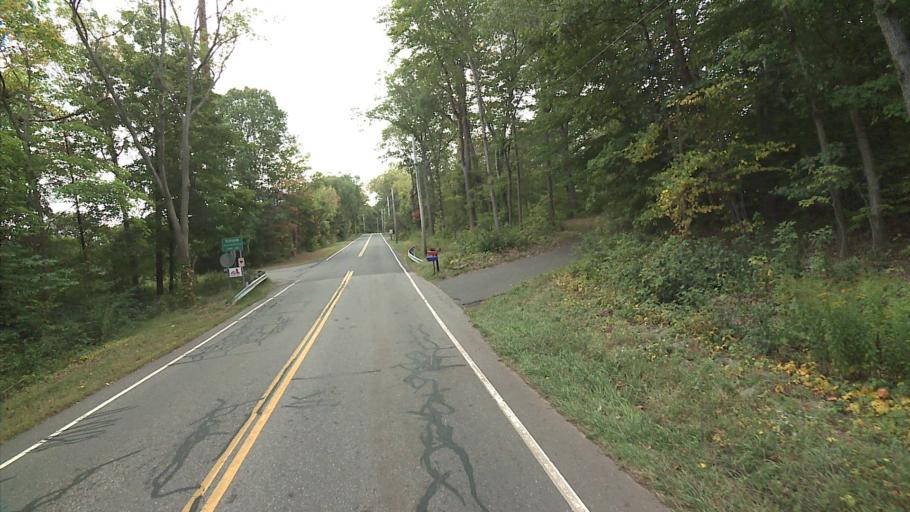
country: US
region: Connecticut
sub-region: Middlesex County
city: Durham
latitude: 41.4882
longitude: -72.7225
